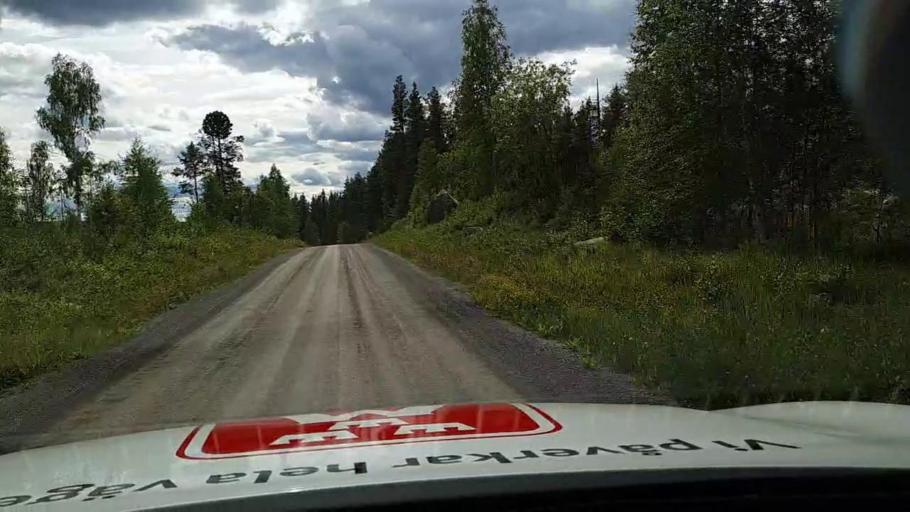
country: SE
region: Jaemtland
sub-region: Braecke Kommun
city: Braecke
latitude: 63.2251
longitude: 15.3471
